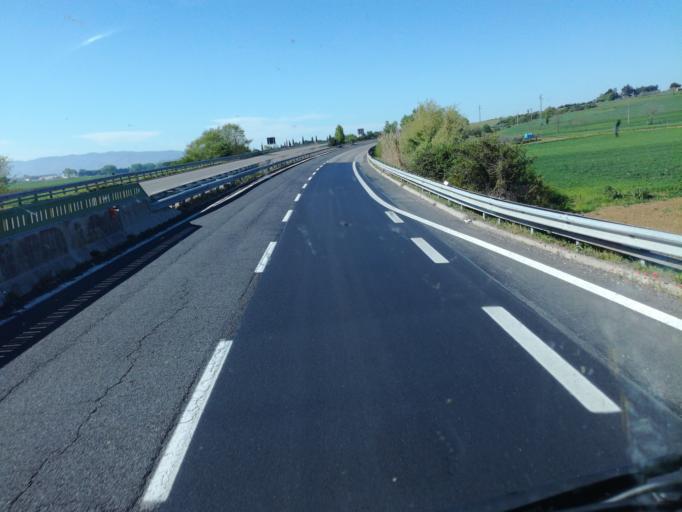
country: IT
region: Umbria
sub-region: Provincia di Perugia
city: Petrignano
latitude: 43.1136
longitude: 12.5071
